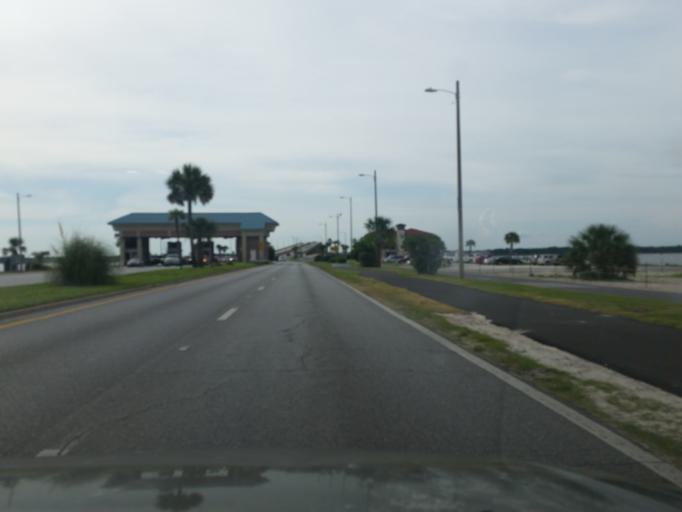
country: US
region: Florida
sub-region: Santa Rosa County
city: Gulf Breeze
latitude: 30.3410
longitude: -87.1480
